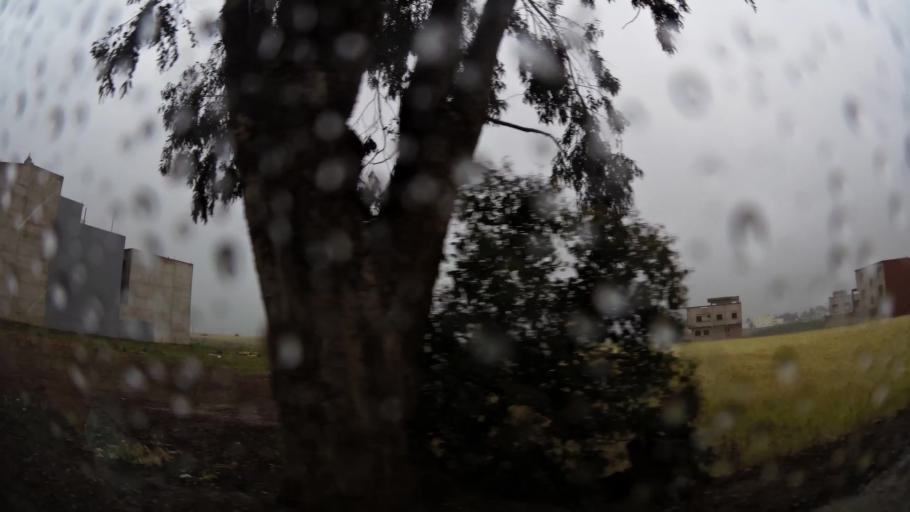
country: MA
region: Oriental
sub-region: Nador
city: Boudinar
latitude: 35.1229
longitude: -3.6459
